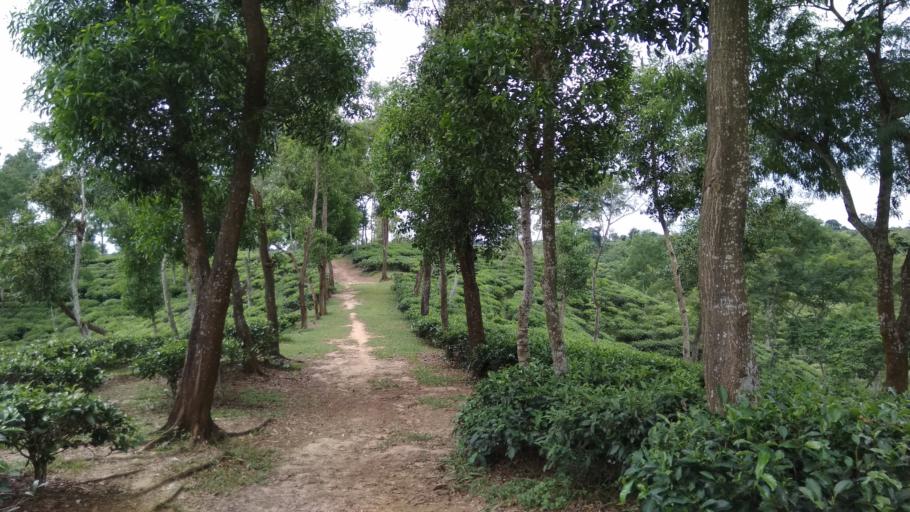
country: IN
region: Tripura
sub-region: Dhalai
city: Kamalpur
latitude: 24.2797
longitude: 91.8200
